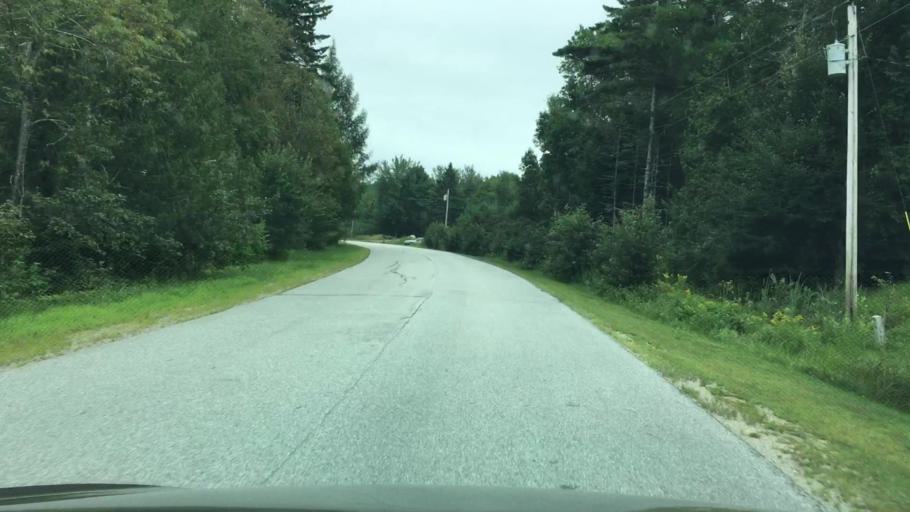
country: US
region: Maine
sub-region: Waldo County
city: Stockton Springs
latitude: 44.5261
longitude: -68.8250
